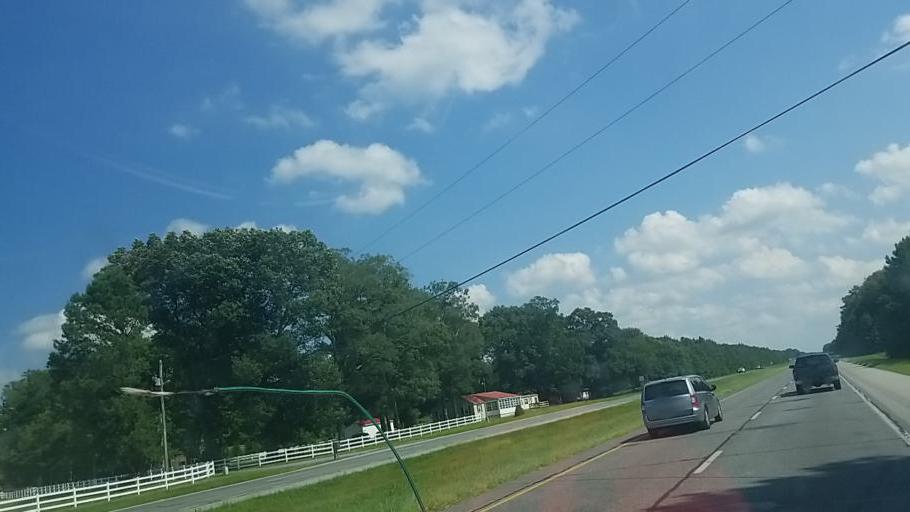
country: US
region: Delaware
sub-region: Sussex County
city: Georgetown
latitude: 38.7479
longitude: -75.4312
